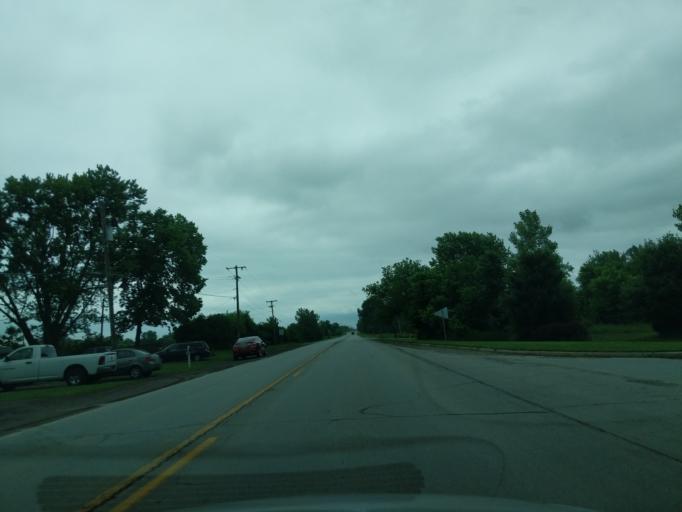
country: US
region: Indiana
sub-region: Hamilton County
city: Noblesville
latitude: 40.0797
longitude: -86.0144
